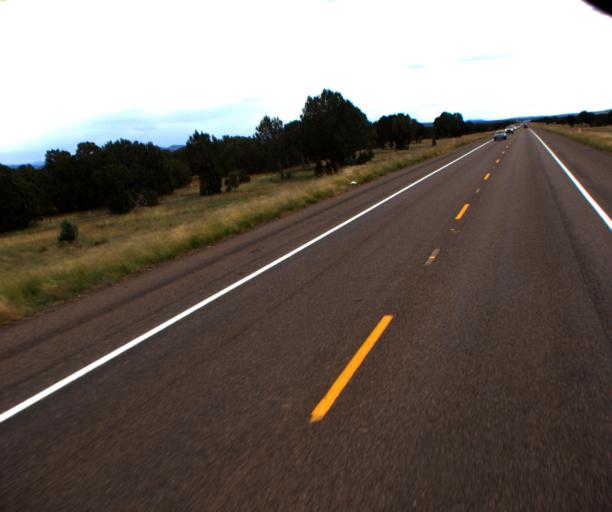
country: US
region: Arizona
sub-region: Navajo County
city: Show Low
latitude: 34.2954
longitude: -110.0330
